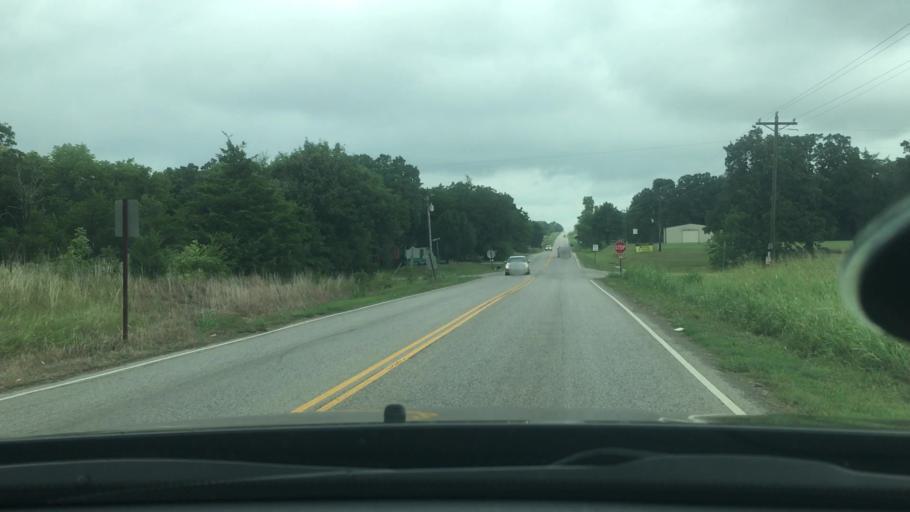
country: US
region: Oklahoma
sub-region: Bryan County
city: Calera
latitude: 33.9394
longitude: -96.5005
